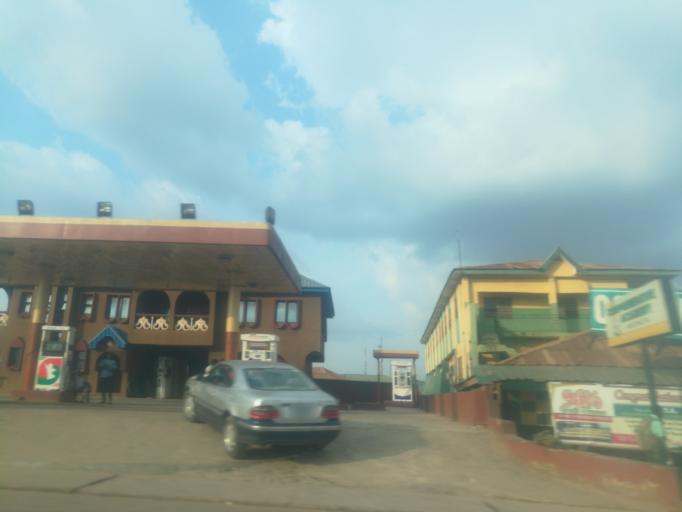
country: NG
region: Ogun
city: Abeokuta
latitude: 7.1624
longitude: 3.3170
